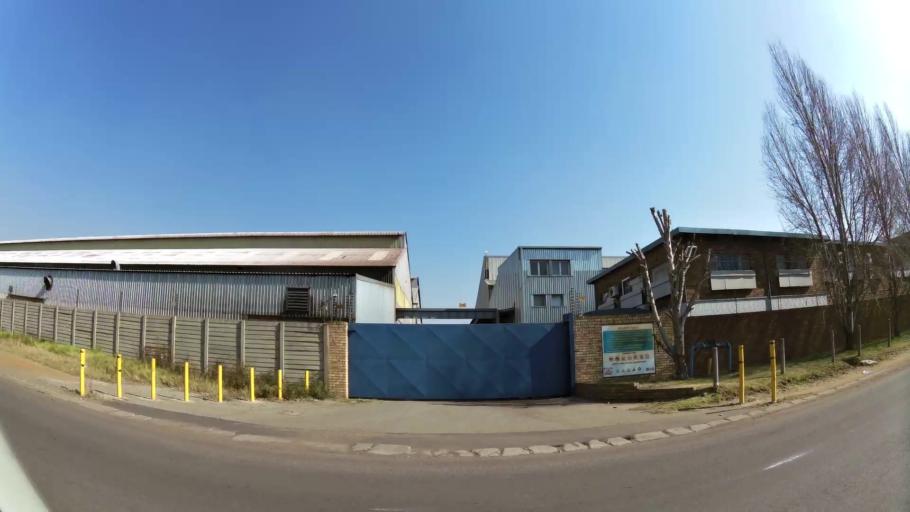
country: ZA
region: Gauteng
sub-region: Ekurhuleni Metropolitan Municipality
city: Benoni
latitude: -26.2079
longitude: 28.3004
